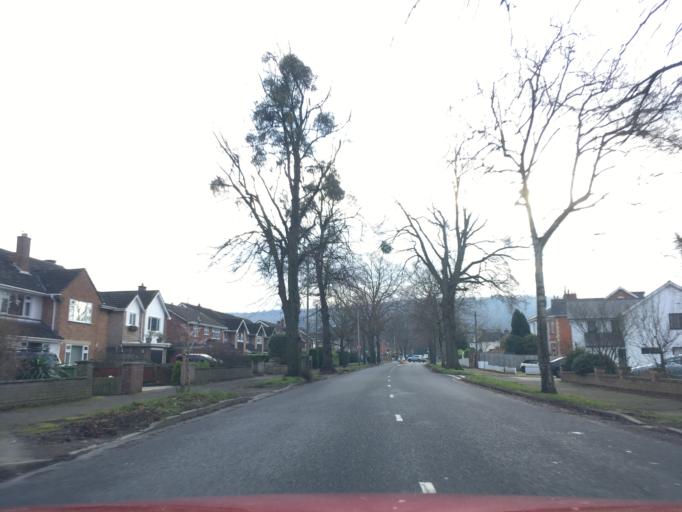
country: GB
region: England
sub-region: Gloucestershire
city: Cheltenham
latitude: 51.8815
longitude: -2.0783
